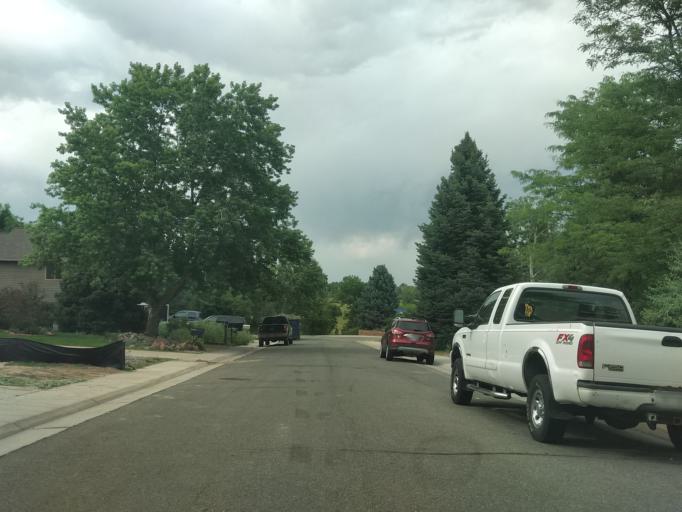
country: US
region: Colorado
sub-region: Jefferson County
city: Lakewood
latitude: 39.6989
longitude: -105.0905
